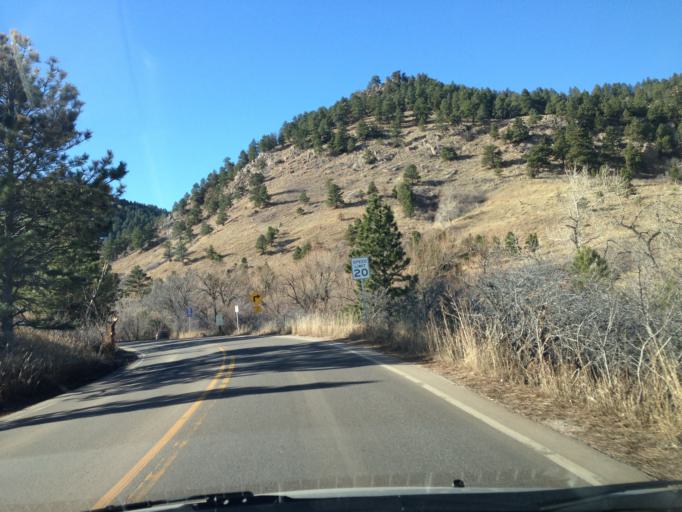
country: US
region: Colorado
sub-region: Boulder County
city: Boulder
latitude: 39.9998
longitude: -105.2891
